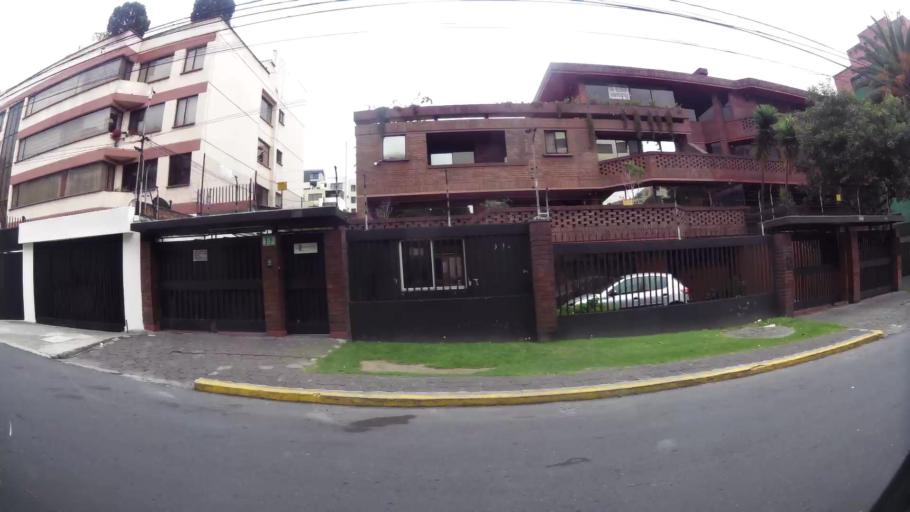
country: EC
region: Pichincha
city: Quito
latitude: -0.1642
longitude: -78.4895
